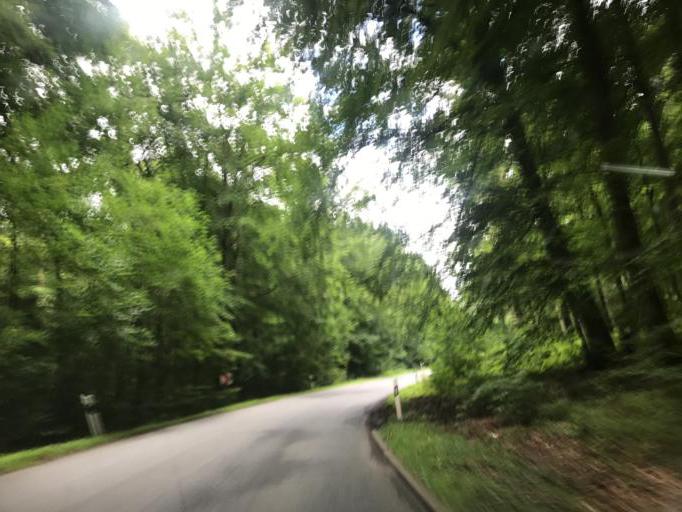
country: DE
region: Mecklenburg-Vorpommern
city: Rechlin
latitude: 53.2370
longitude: 12.7018
